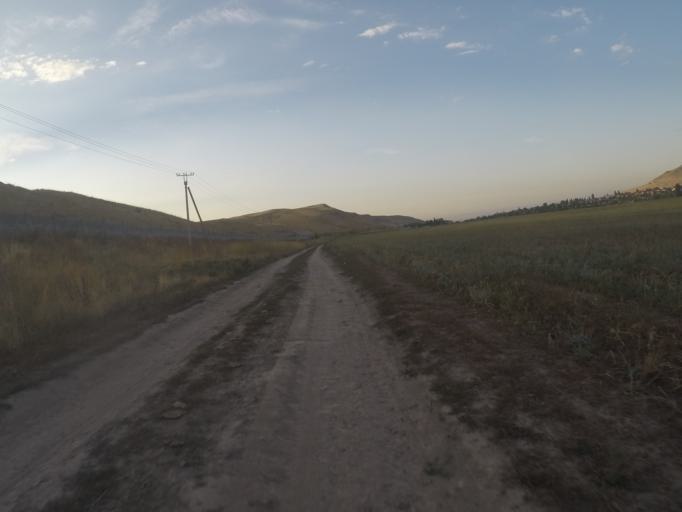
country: KG
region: Chuy
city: Bishkek
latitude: 42.7564
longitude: 74.6362
